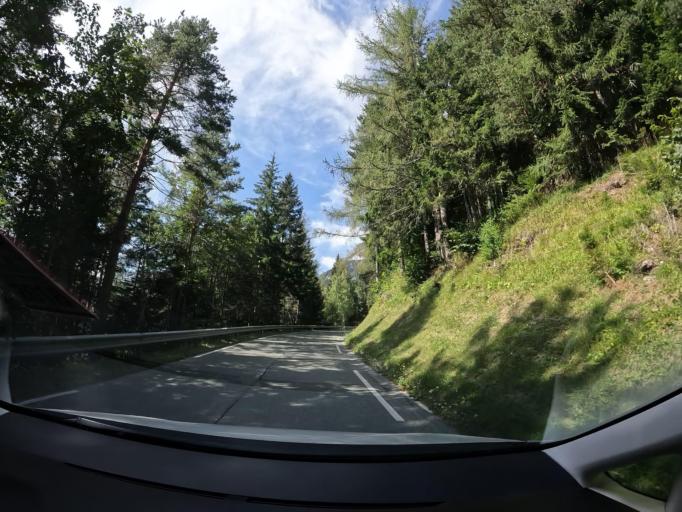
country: AT
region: Carinthia
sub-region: Politischer Bezirk Feldkirchen
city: Glanegg
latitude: 46.7374
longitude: 14.2108
